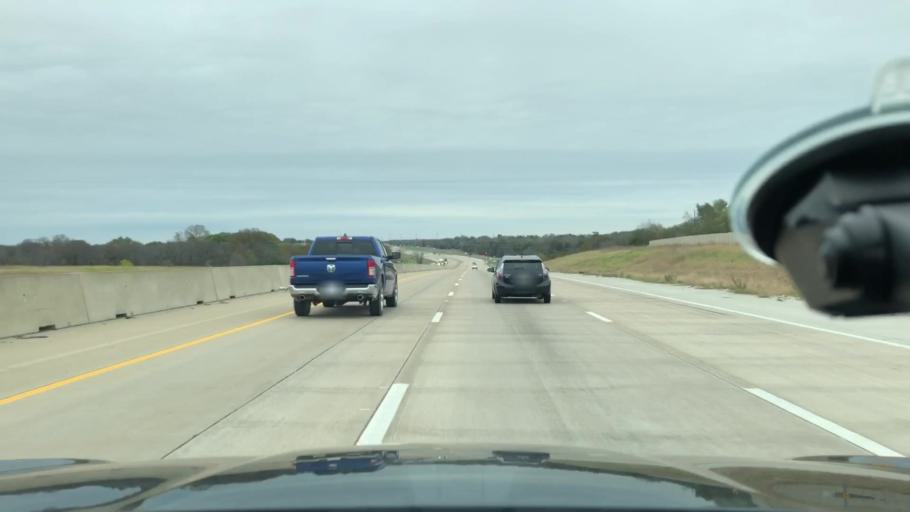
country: US
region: Texas
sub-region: Ellis County
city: Waxahachie
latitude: 32.3411
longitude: -96.8559
